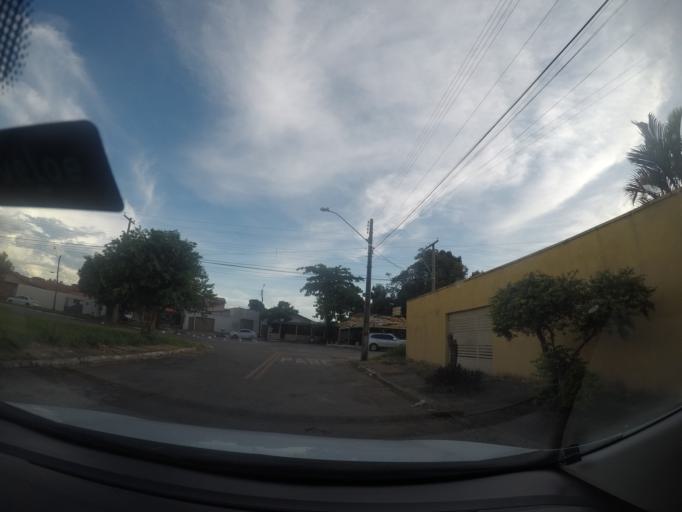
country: BR
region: Goias
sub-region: Goiania
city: Goiania
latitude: -16.6856
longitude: -49.3173
